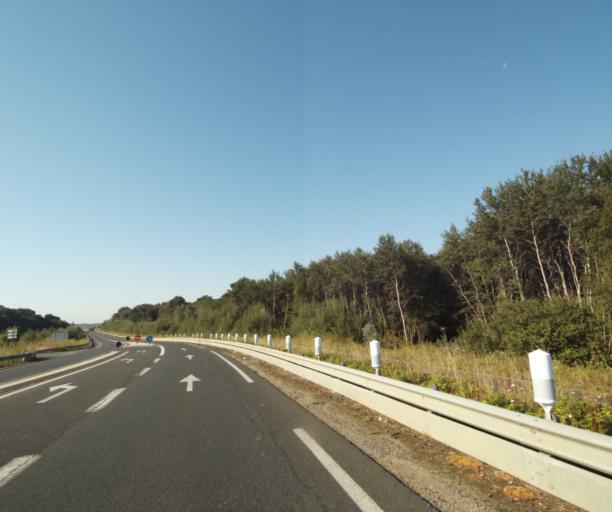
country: FR
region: Ile-de-France
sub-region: Departement de Seine-et-Marne
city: Moissy-Cramayel
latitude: 48.5975
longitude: 2.6042
